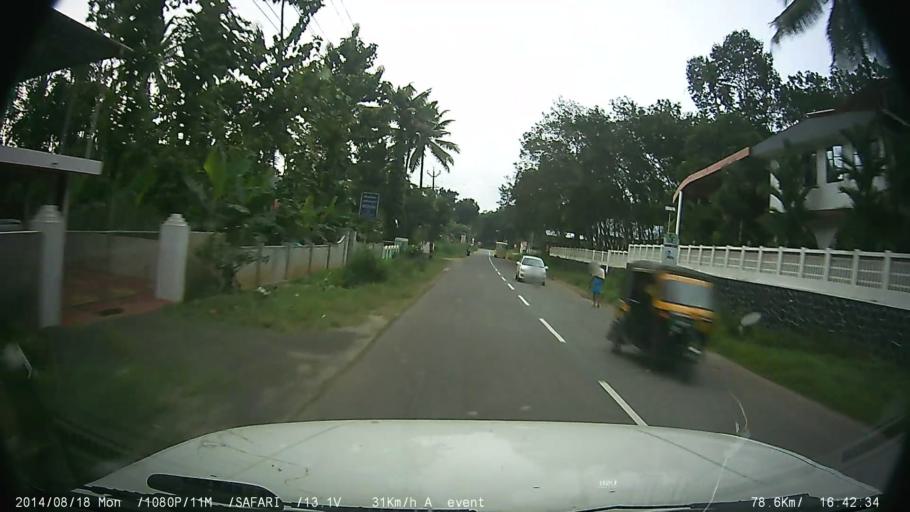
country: IN
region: Kerala
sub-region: Ernakulam
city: Piravam
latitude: 9.8432
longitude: 76.5918
